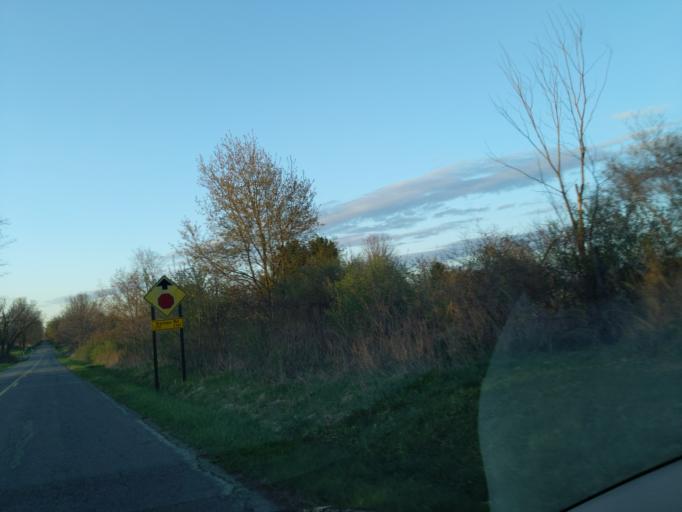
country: US
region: Michigan
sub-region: Ingham County
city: Mason
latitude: 42.5223
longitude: -84.4526
